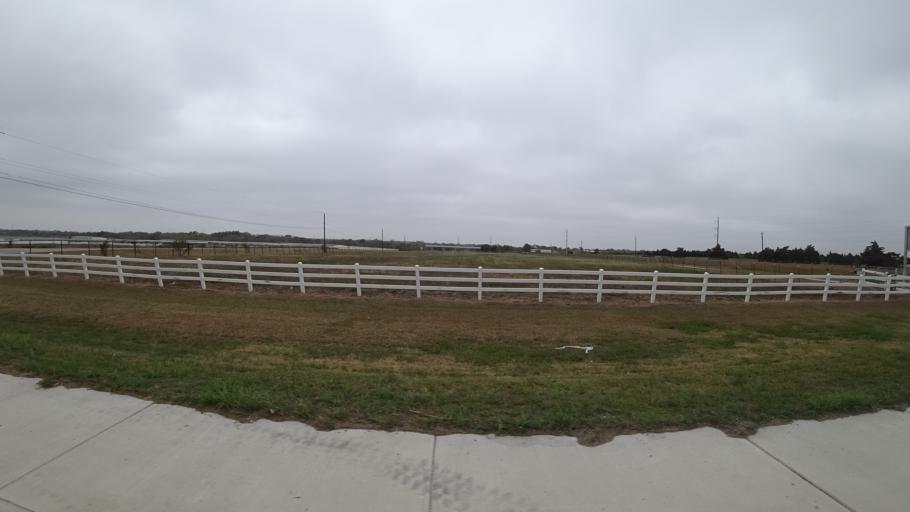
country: US
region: Texas
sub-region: Travis County
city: Manor
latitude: 30.3758
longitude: -97.6099
